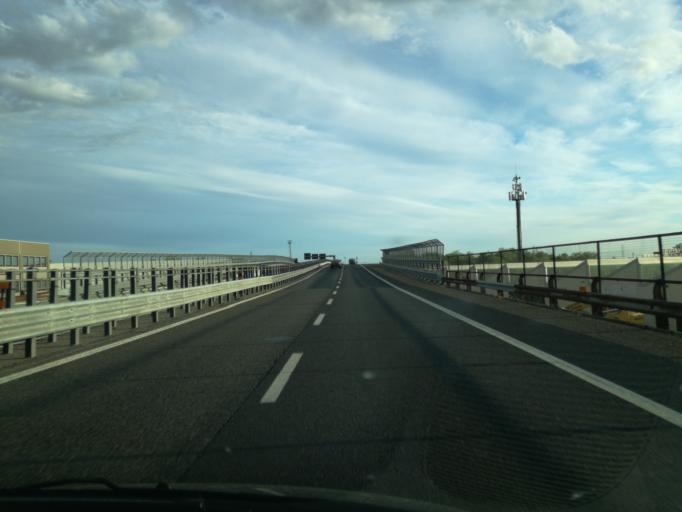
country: IT
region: Lombardy
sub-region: Provincia di Monza e Brianza
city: Agrate Brianza
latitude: 45.5677
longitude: 9.3367
